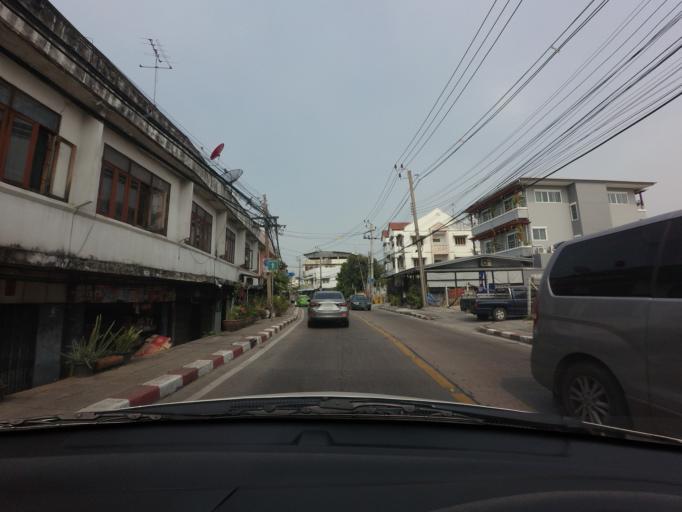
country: TH
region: Bangkok
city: Taling Chan
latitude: 13.7797
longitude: 100.4652
